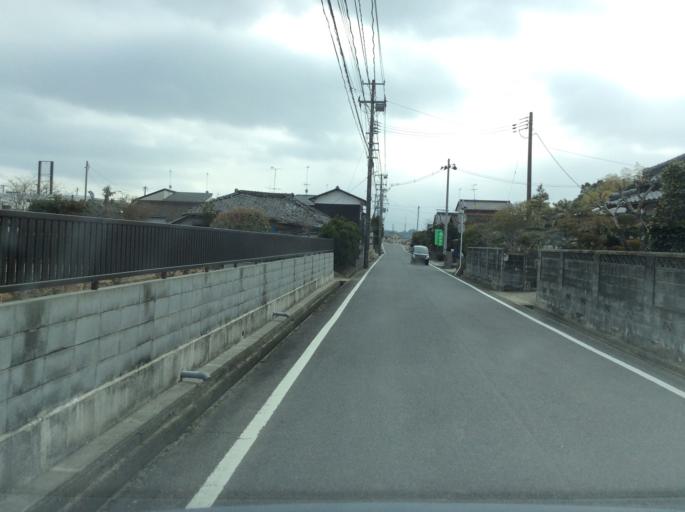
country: JP
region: Fukushima
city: Iwaki
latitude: 37.0799
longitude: 140.9594
